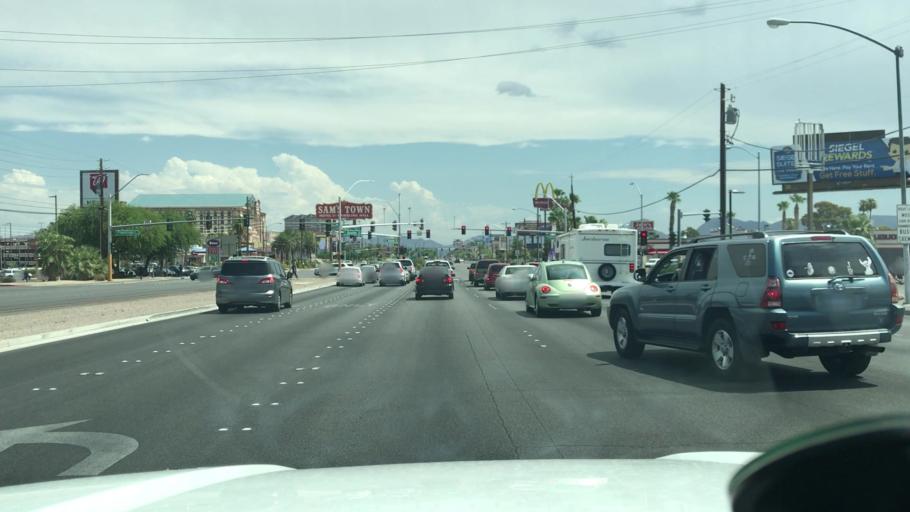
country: US
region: Nevada
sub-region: Clark County
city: Whitney
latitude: 36.1156
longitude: -115.0677
